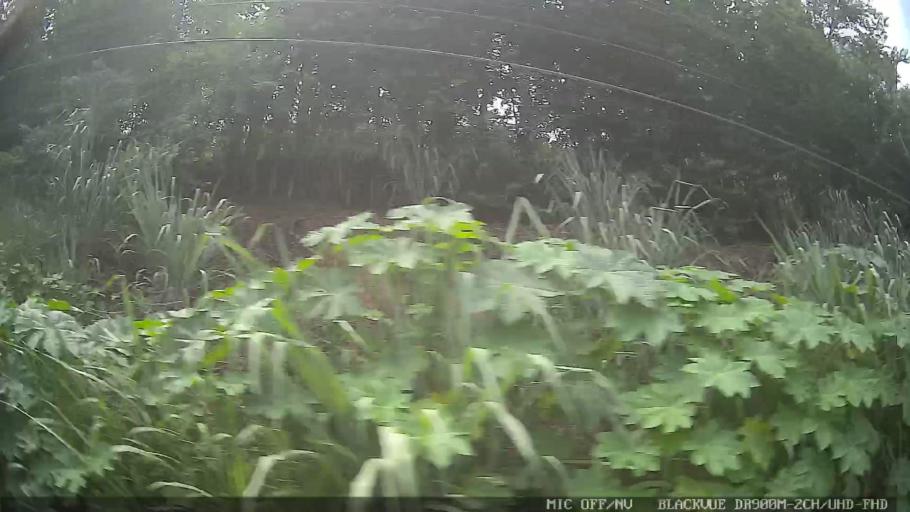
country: BR
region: Sao Paulo
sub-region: Santa Isabel
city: Santa Isabel
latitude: -23.4191
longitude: -46.2173
